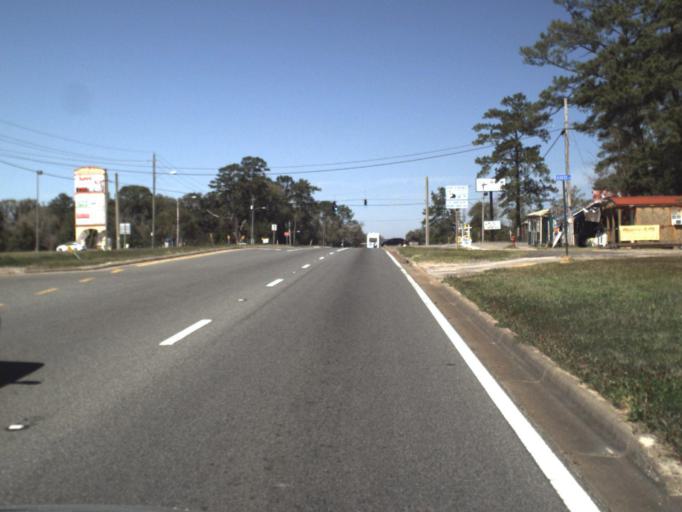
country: US
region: Florida
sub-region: Jackson County
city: Marianna
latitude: 30.7617
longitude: -85.1993
